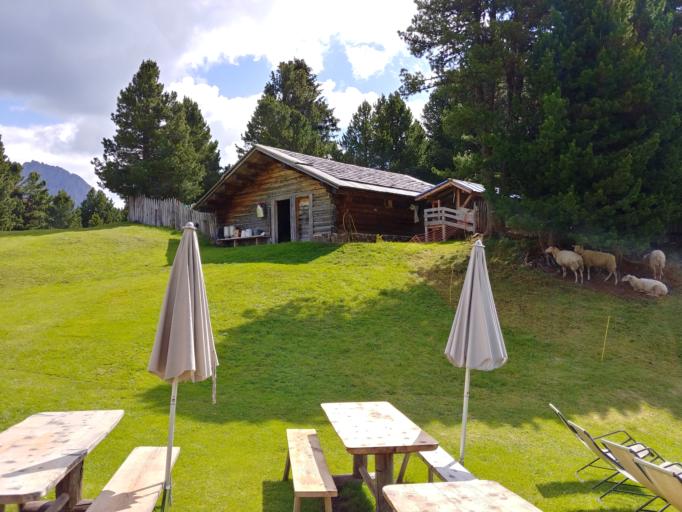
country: IT
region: Trentino-Alto Adige
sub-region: Bolzano
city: Santa Cristina Valgardena
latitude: 46.5856
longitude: 11.7296
